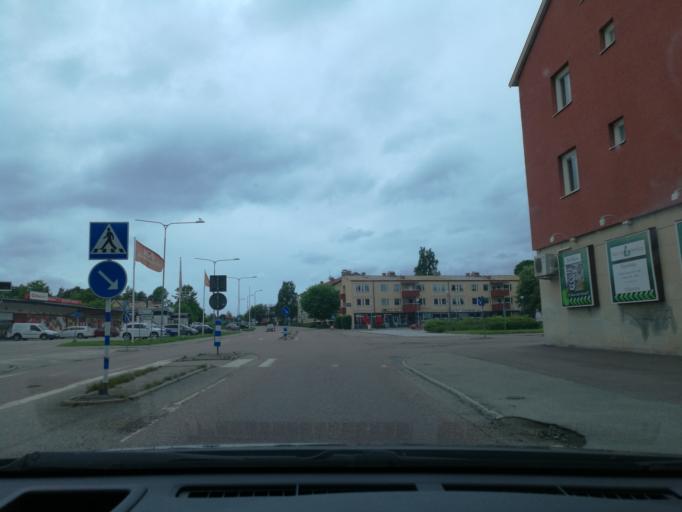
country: SE
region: Dalarna
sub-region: Ludvika Kommun
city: Ludvika
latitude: 60.1507
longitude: 15.2027
